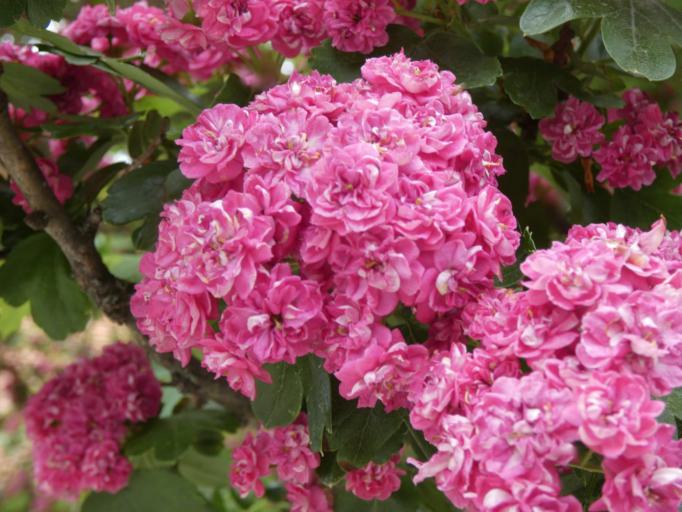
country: HU
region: Pest
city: Pilisborosjeno
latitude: 47.6141
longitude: 18.9929
